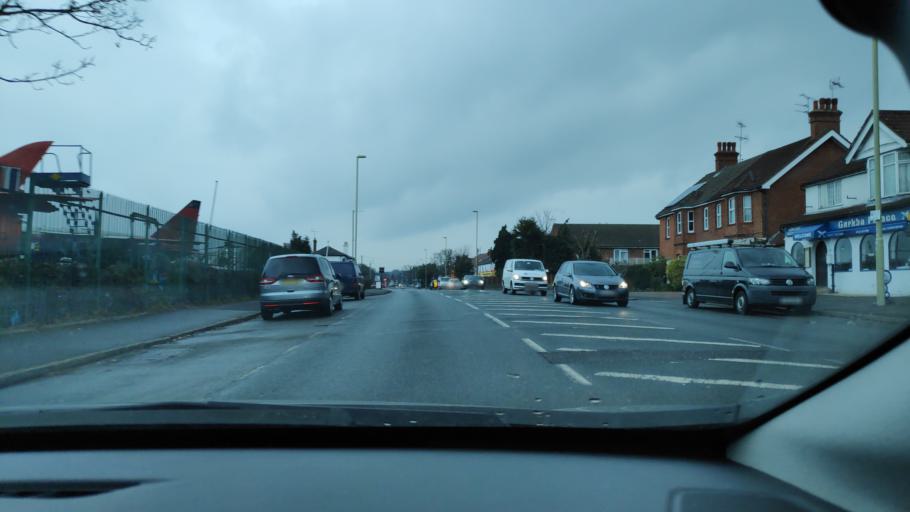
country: GB
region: England
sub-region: Hampshire
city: Farnborough
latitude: 51.2820
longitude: -0.7531
